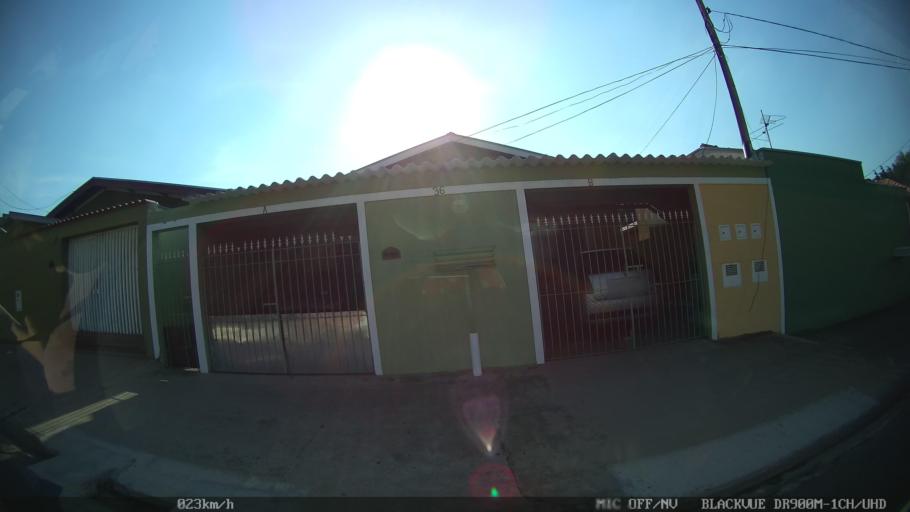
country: BR
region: Sao Paulo
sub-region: Indaiatuba
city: Indaiatuba
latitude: -22.9897
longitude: -47.1500
